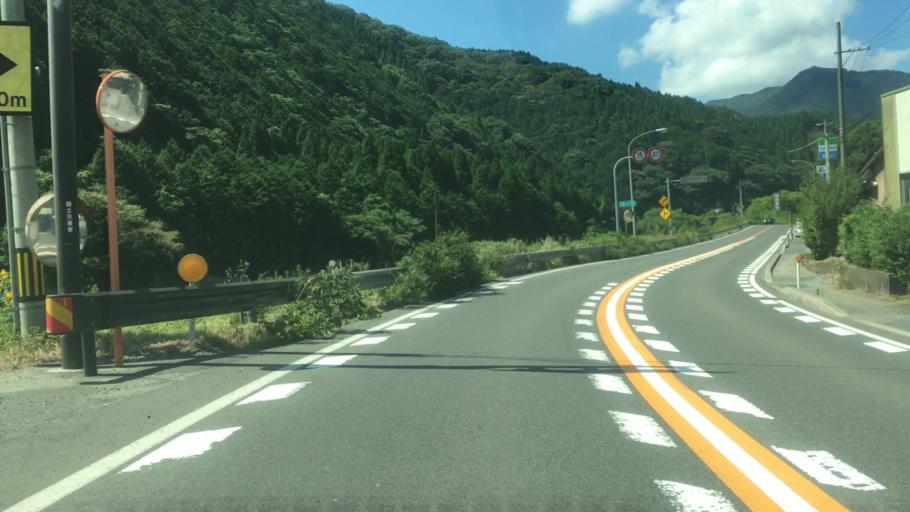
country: JP
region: Tottori
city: Tottori
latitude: 35.2727
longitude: 134.2241
